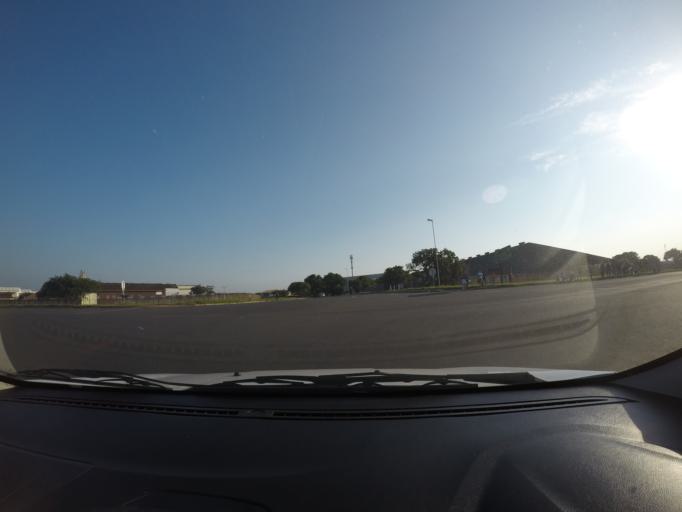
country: ZA
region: KwaZulu-Natal
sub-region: uThungulu District Municipality
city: Richards Bay
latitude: -28.7674
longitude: 32.0092
